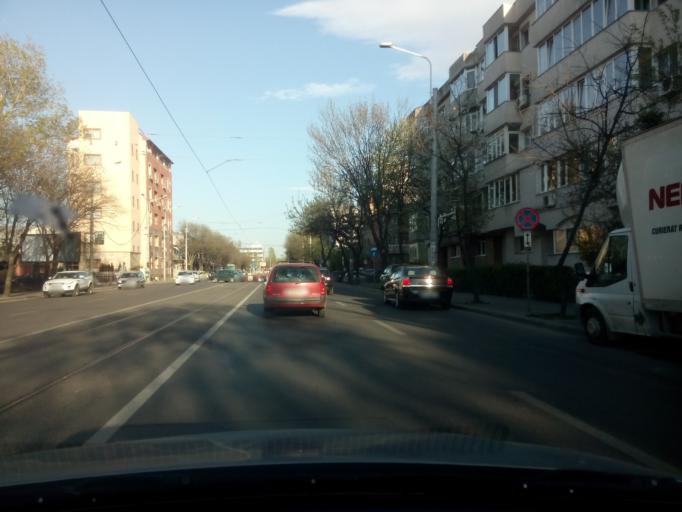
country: RO
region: Ilfov
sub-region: Comuna Otopeni
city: Otopeni
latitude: 44.4942
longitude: 26.0813
